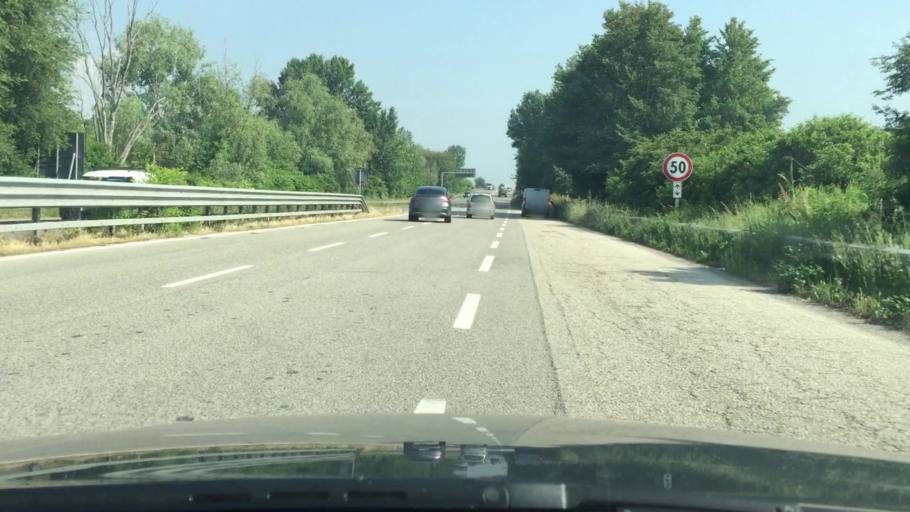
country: IT
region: Emilia-Romagna
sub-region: Provincia di Ferrara
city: Gaibanella-Sant'Edigio
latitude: 44.7975
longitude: 11.6371
